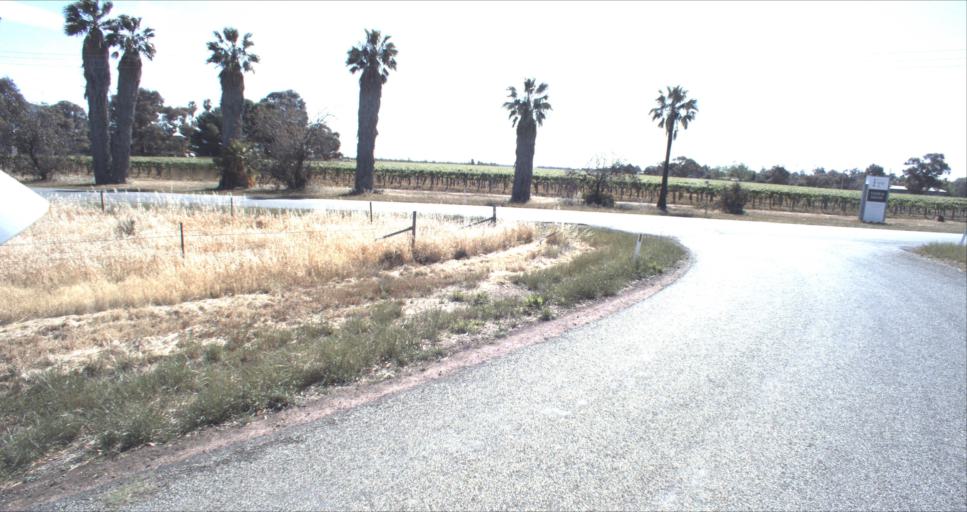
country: AU
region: New South Wales
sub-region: Leeton
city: Leeton
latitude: -34.5564
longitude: 146.3847
